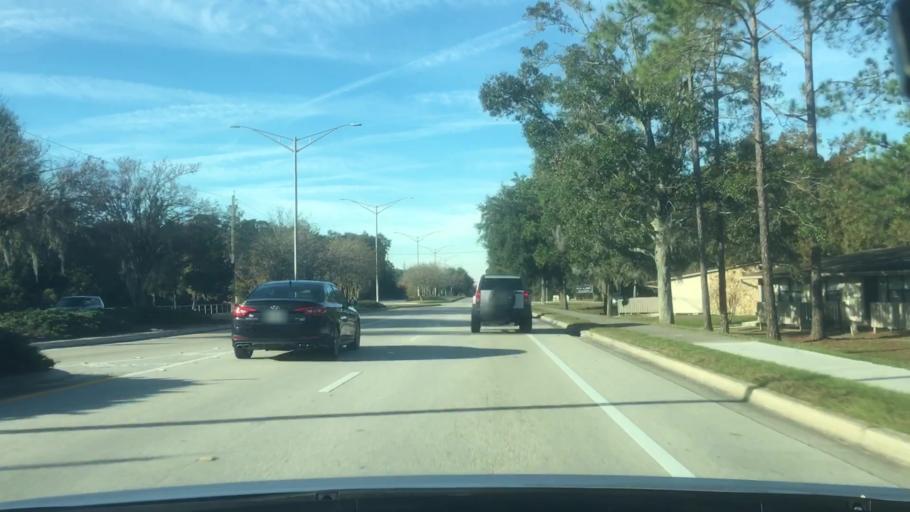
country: US
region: Florida
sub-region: Duval County
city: Atlantic Beach
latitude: 30.3471
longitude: -81.5260
